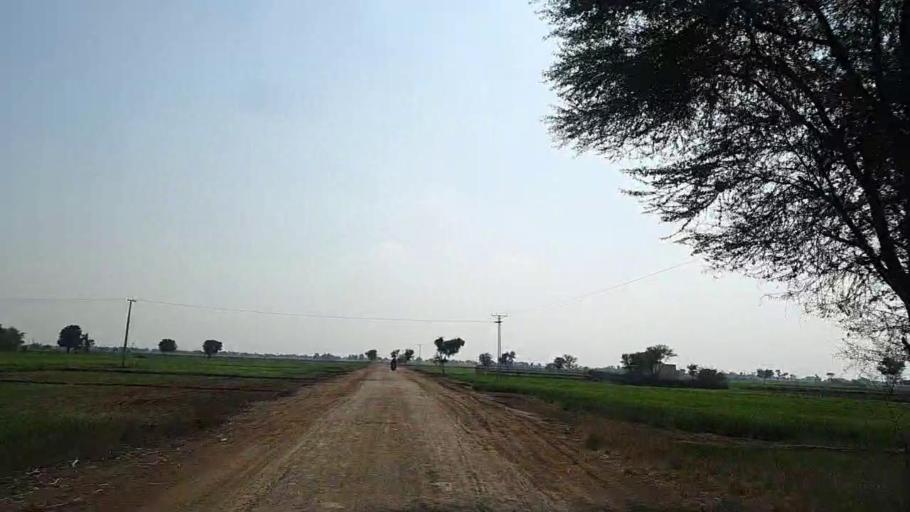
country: PK
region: Sindh
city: Daur
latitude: 26.4479
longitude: 68.2347
